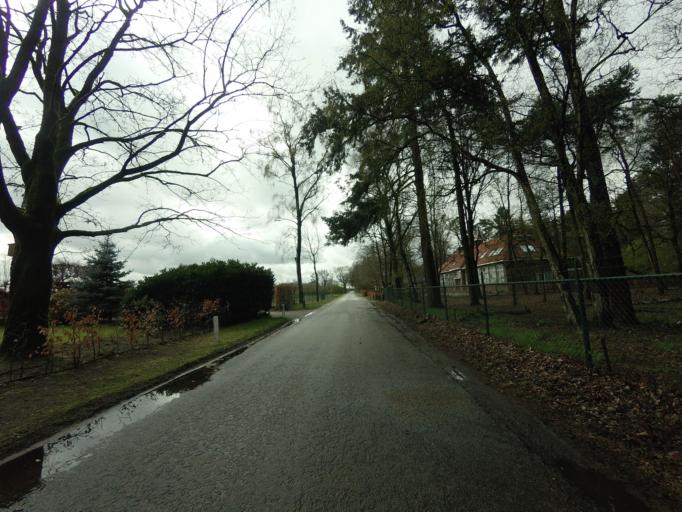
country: NL
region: Gelderland
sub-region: Gemeente Barneveld
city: Stroe
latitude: 52.1847
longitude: 5.6792
